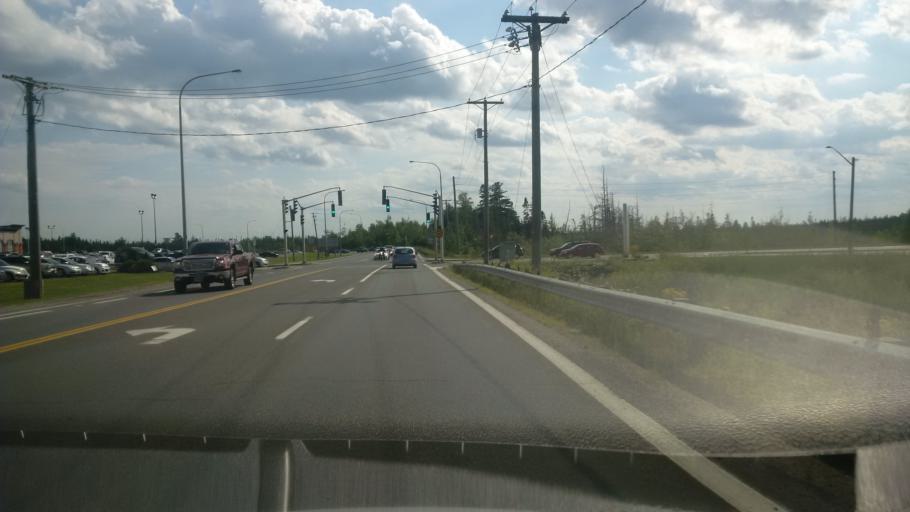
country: CA
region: New Brunswick
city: Fredericton
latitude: 45.9371
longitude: -66.6661
